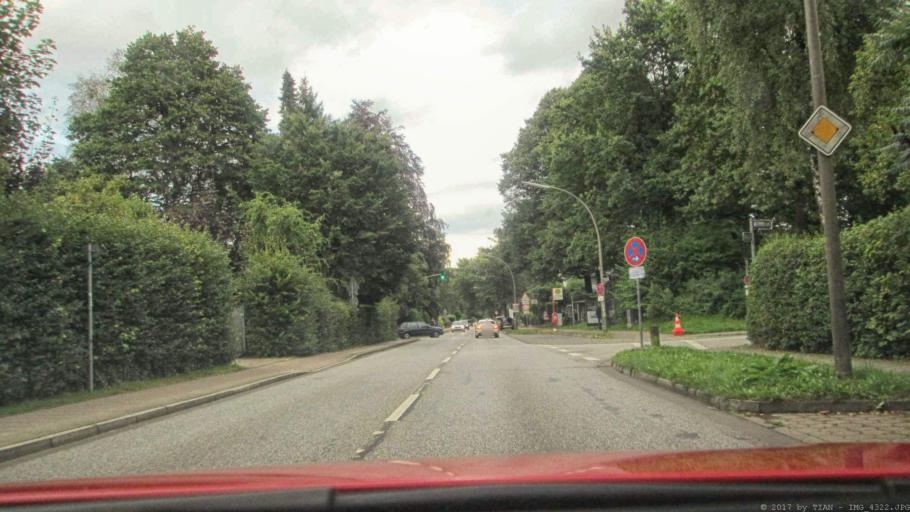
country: DE
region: Schleswig-Holstein
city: Halstenbek
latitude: 53.5656
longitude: 9.8007
